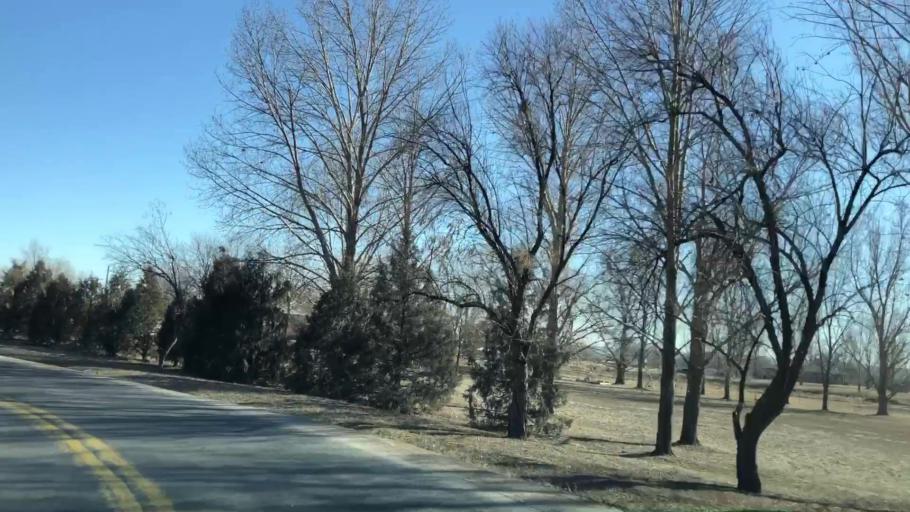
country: US
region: Colorado
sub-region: Weld County
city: Windsor
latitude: 40.4900
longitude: -104.9440
